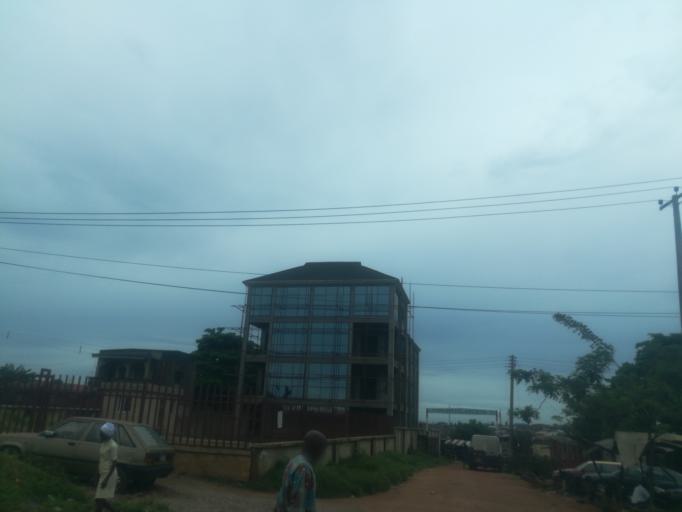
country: NG
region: Oyo
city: Ibadan
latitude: 7.3396
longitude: 3.9056
